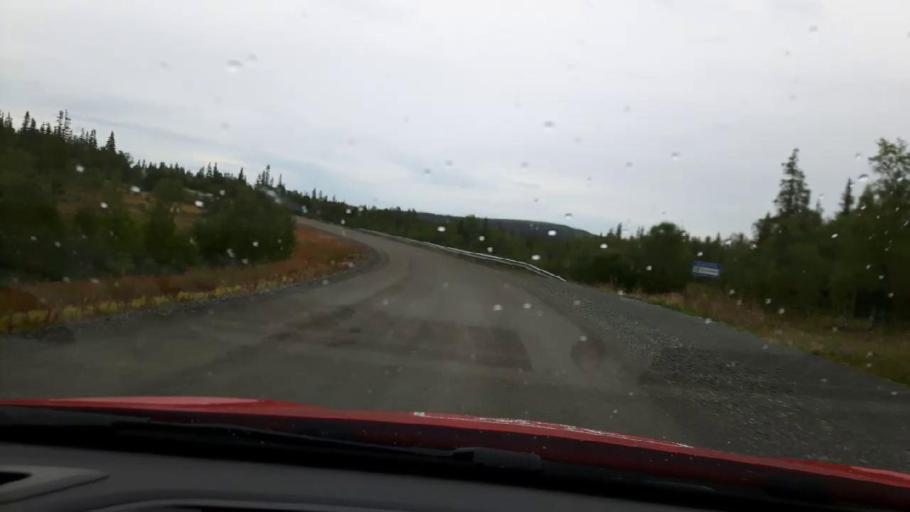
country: NO
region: Nord-Trondelag
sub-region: Meraker
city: Meraker
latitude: 63.5559
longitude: 12.3232
